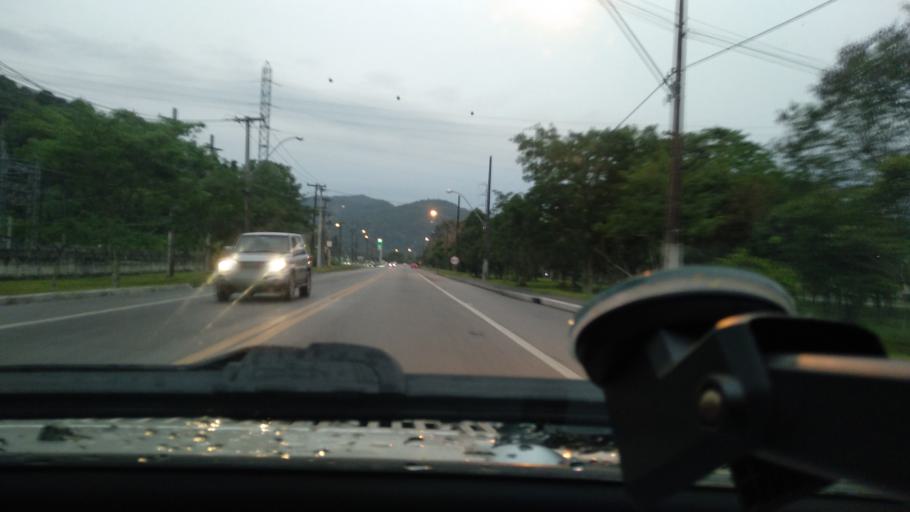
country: BR
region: Rio de Janeiro
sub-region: Angra Dos Reis
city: Angra dos Reis
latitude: -23.0294
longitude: -44.5431
